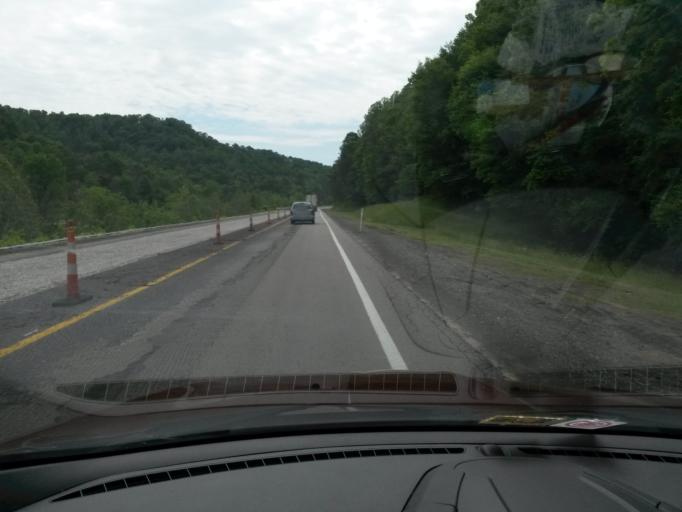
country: US
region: West Virginia
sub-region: Braxton County
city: Sutton
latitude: 38.7352
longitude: -80.6769
